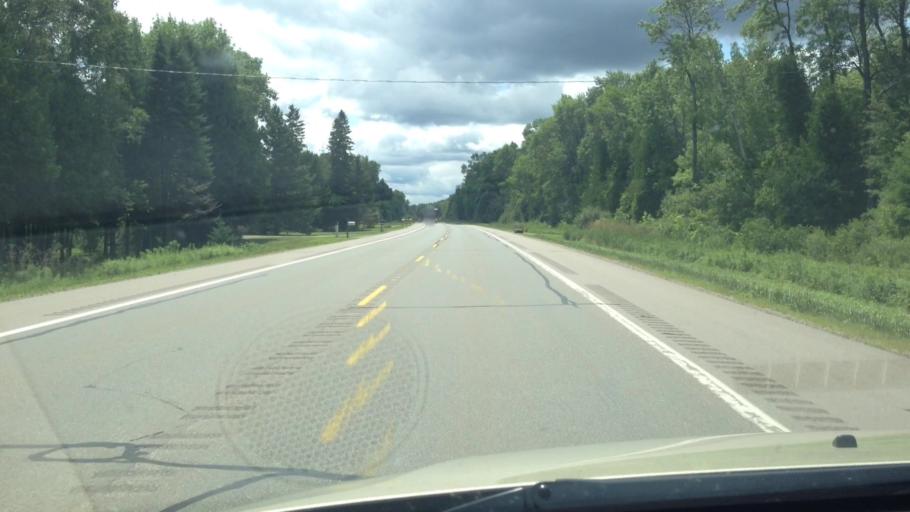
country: US
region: Michigan
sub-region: Menominee County
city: Menominee
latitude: 45.2385
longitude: -87.5009
